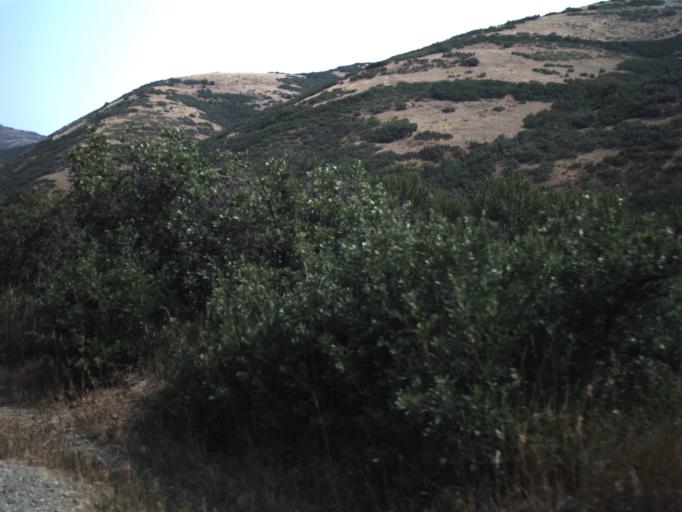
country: US
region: Utah
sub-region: Summit County
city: Summit Park
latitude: 40.7927
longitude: -111.6807
